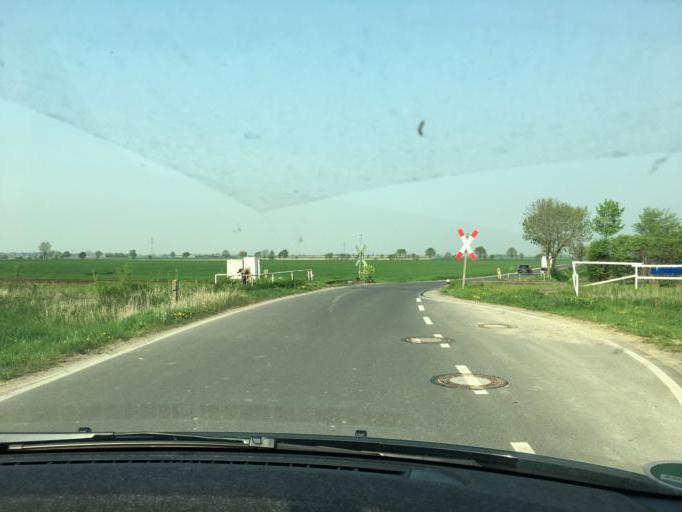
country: DE
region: North Rhine-Westphalia
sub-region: Regierungsbezirk Koln
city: Vettweiss
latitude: 50.7666
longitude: 6.5648
